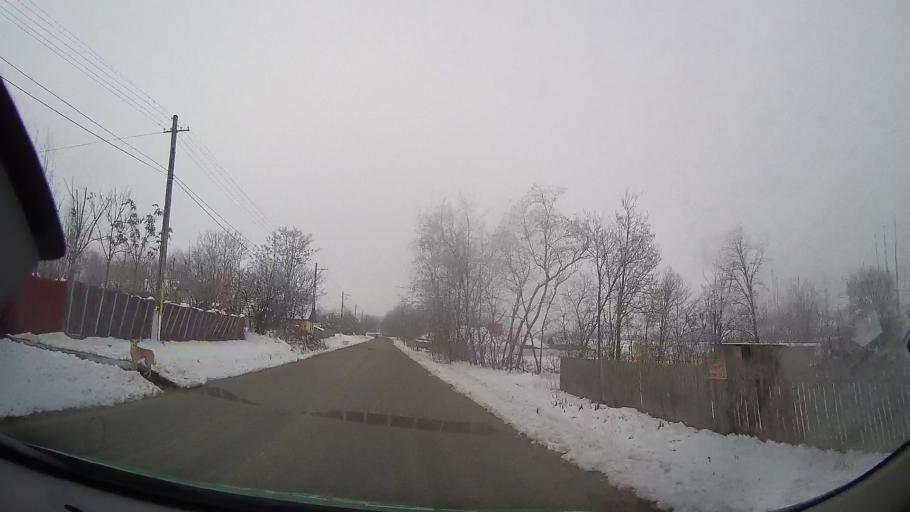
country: RO
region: Bacau
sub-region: Comuna Oncesti
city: Oncesti
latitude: 46.4430
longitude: 27.2660
